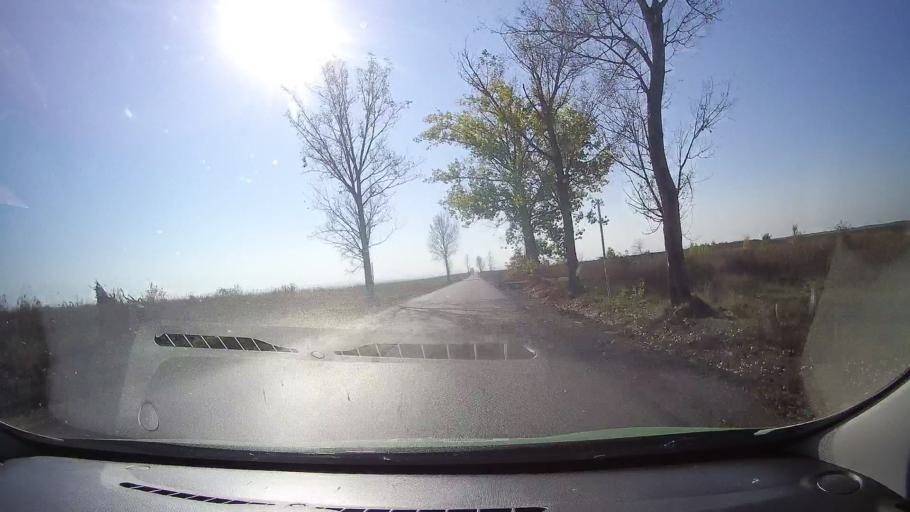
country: RO
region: Satu Mare
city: Carei
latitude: 47.6506
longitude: 22.4623
